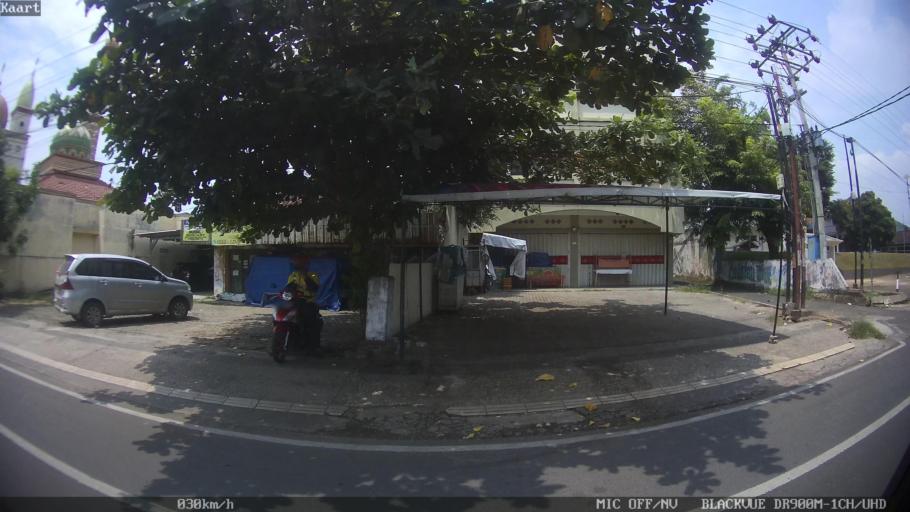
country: ID
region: Lampung
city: Bandarlampung
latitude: -5.4297
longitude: 105.2665
